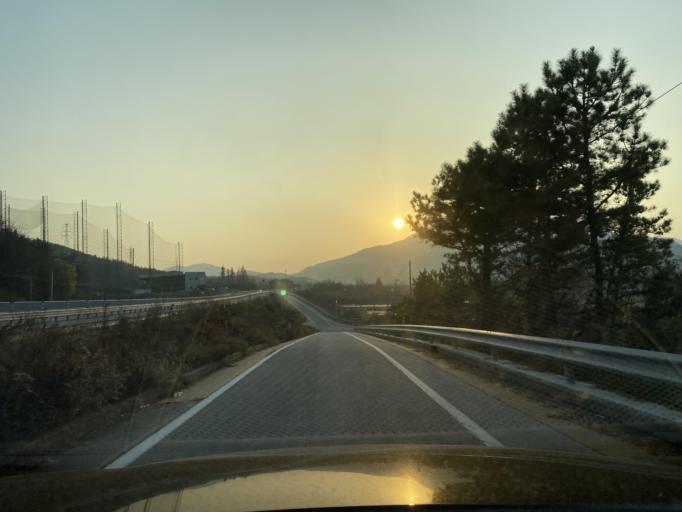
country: KR
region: Chungcheongnam-do
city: Hongsung
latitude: 36.6846
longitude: 126.6600
